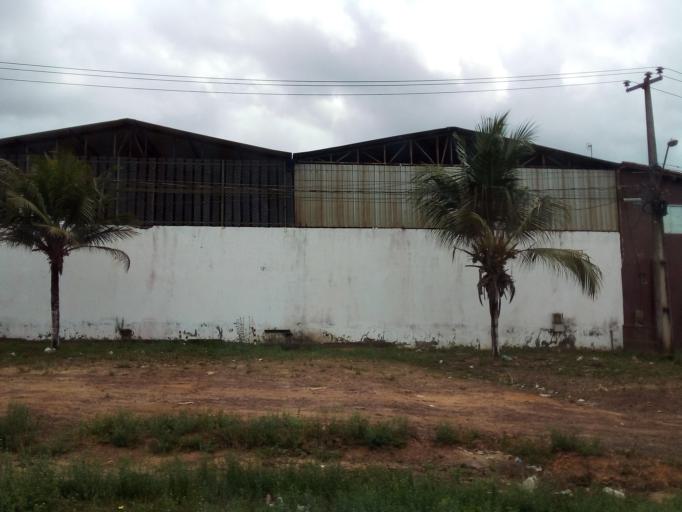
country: BR
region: Maranhao
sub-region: Sao Luis
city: Sao Luis
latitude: -2.6738
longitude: -44.2967
